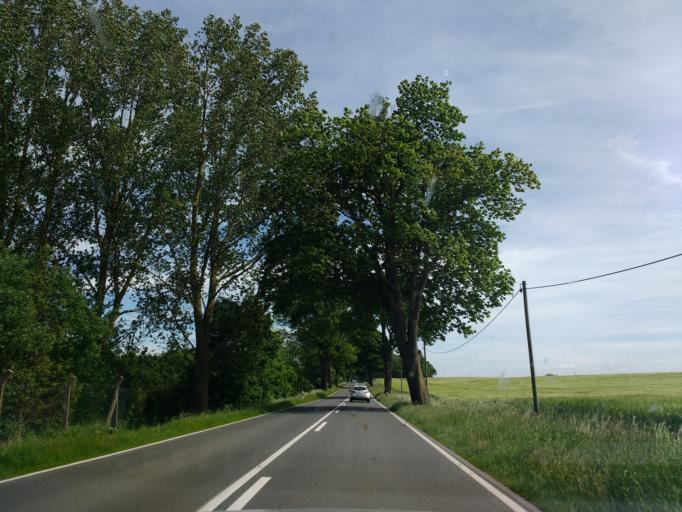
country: DE
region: Mecklenburg-Vorpommern
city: Zurow
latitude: 53.8528
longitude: 11.6289
